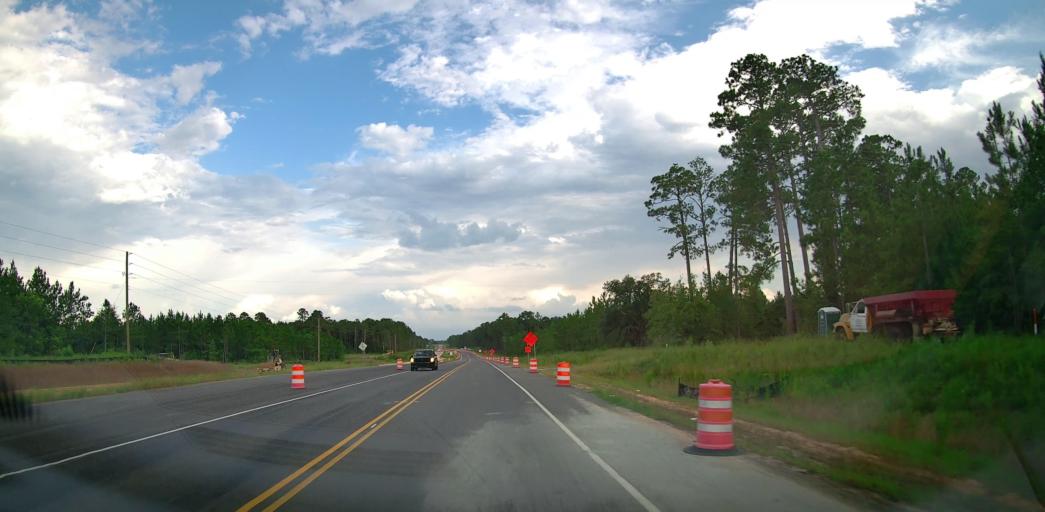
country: US
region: Georgia
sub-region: Dodge County
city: Eastman
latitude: 32.2459
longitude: -83.2374
